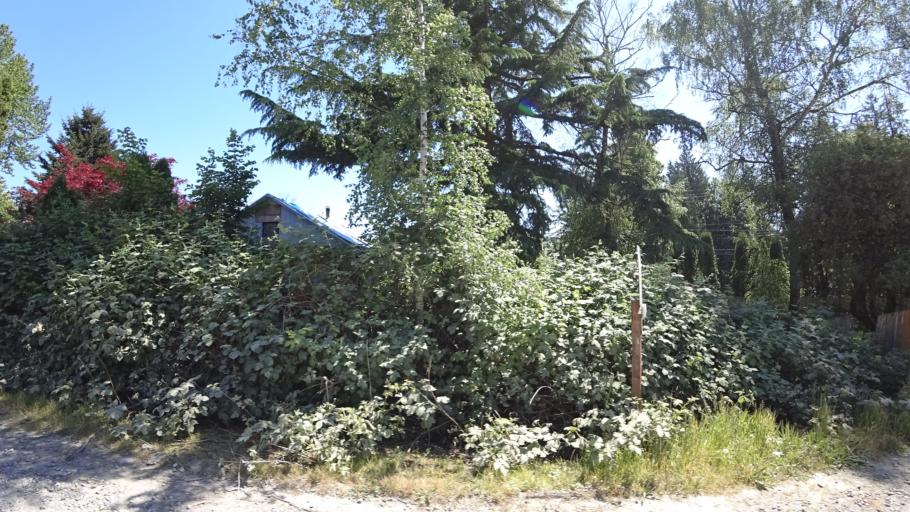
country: US
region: Oregon
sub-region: Clackamas County
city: Happy Valley
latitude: 45.4686
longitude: -122.4879
